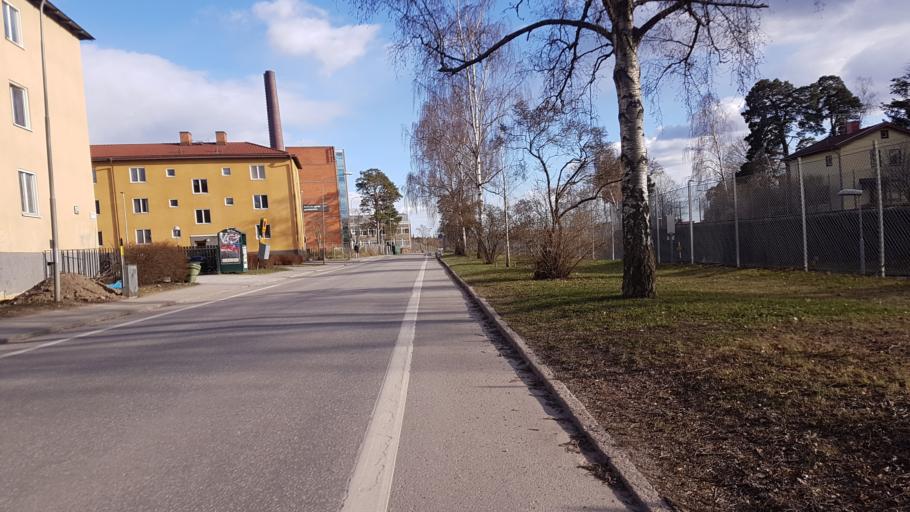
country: SE
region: Stockholm
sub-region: Stockholms Kommun
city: Arsta
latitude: 59.2879
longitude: 18.0719
